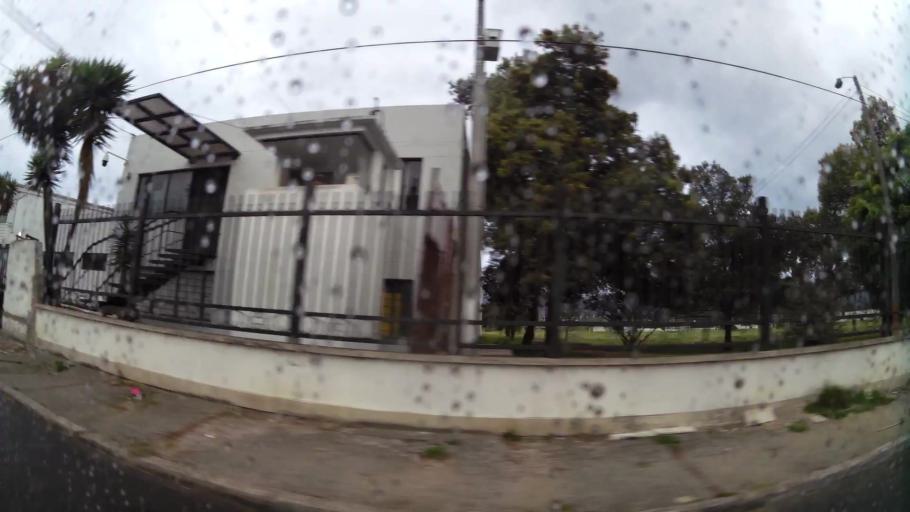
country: CO
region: Bogota D.C.
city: Bogota
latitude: 4.5921
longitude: -74.1346
